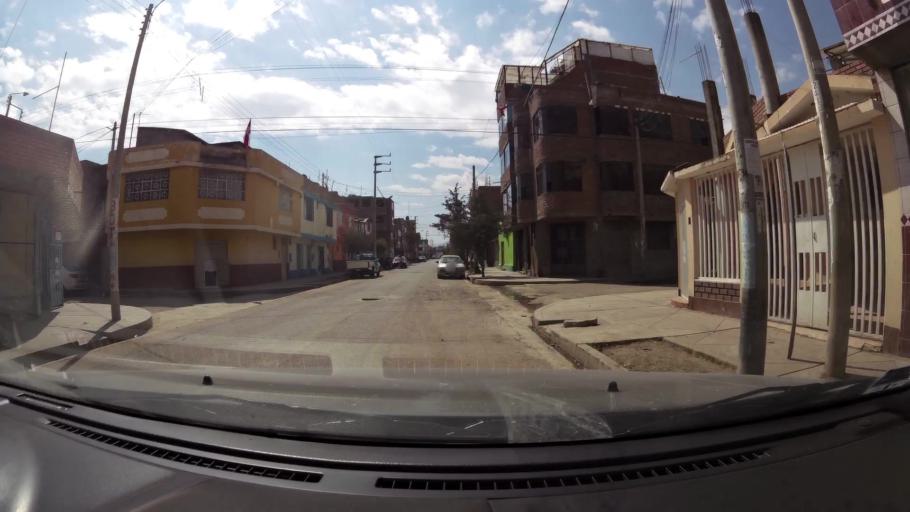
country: PE
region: Junin
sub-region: Provincia de Huancayo
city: Huancayo
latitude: -12.0883
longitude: -75.2059
